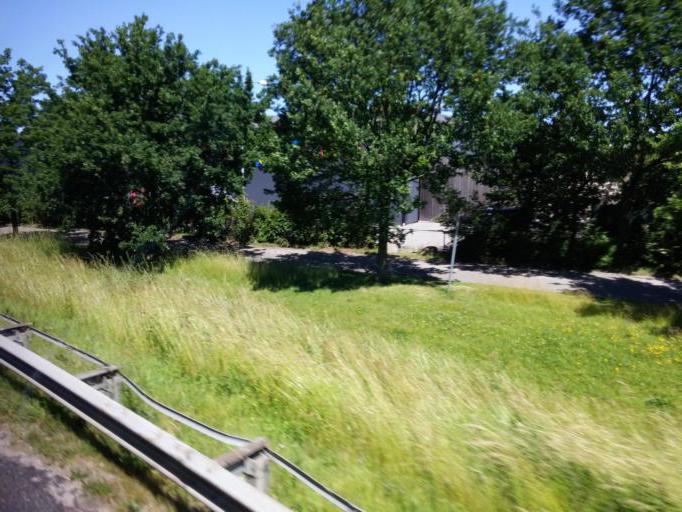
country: SE
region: Skane
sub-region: Malmo
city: Oxie
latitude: 55.5661
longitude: 13.0615
